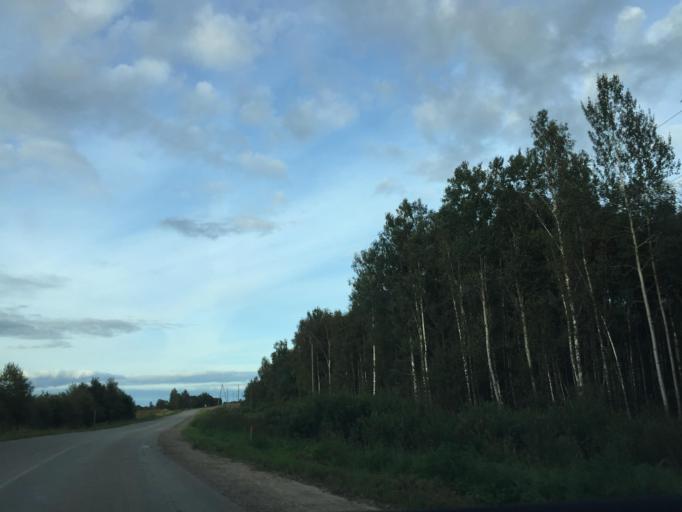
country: LV
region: Nereta
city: Nereta
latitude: 56.2939
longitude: 25.4165
